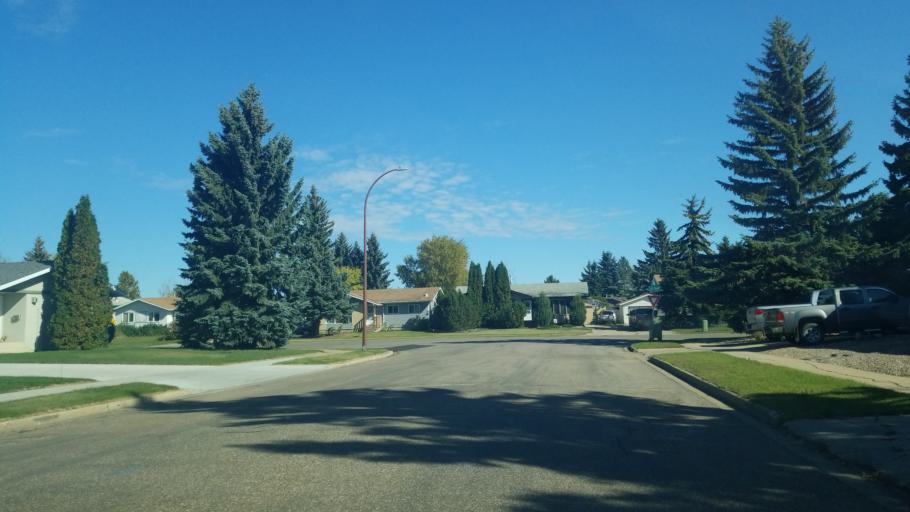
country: CA
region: Saskatchewan
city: Lloydminster
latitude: 53.2748
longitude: -110.0147
